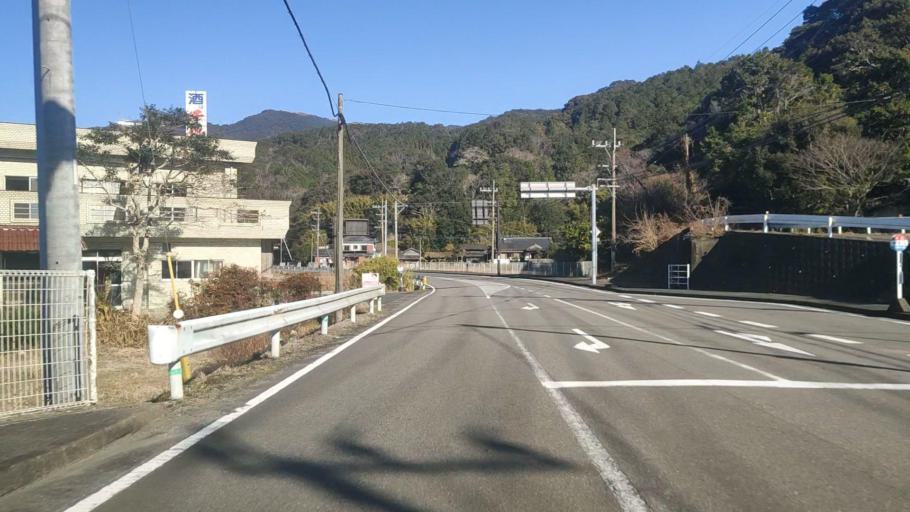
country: JP
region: Miyazaki
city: Nobeoka
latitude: 32.6657
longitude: 131.7667
